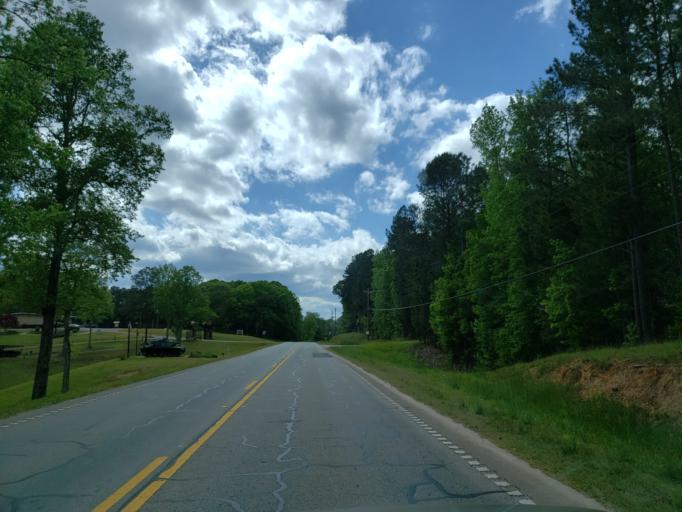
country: US
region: Georgia
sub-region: Haralson County
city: Tallapoosa
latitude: 33.7387
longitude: -85.2638
